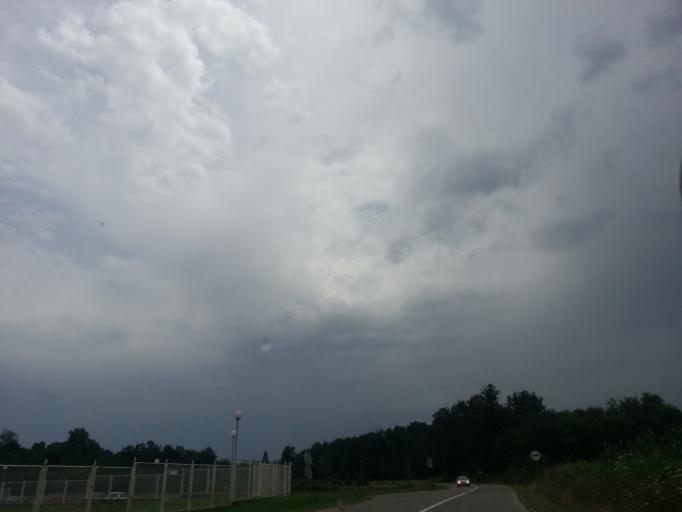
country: BA
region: Republika Srpska
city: Velika Obarska
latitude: 44.7907
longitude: 19.0857
